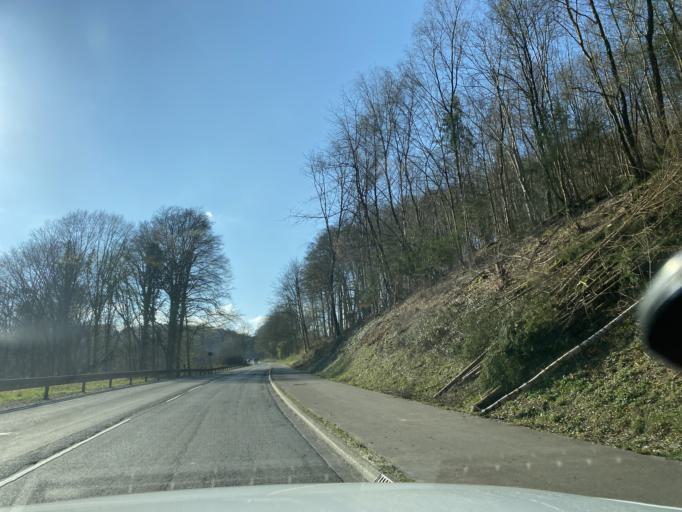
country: DE
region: North Rhine-Westphalia
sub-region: Regierungsbezirk Koln
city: Odenthal
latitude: 51.0251
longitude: 7.1231
